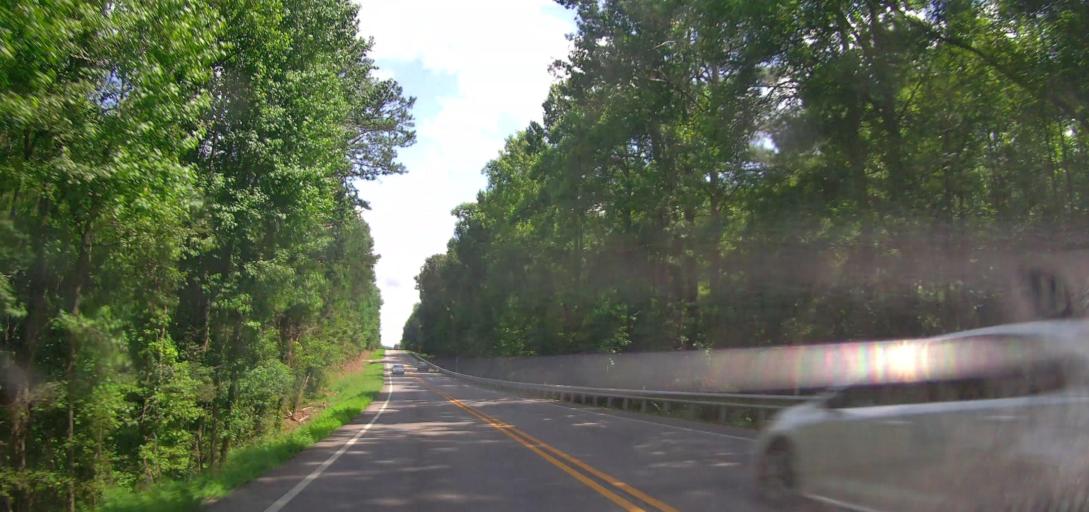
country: US
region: Alabama
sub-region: Cleburne County
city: Heflin
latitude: 33.6331
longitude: -85.4869
